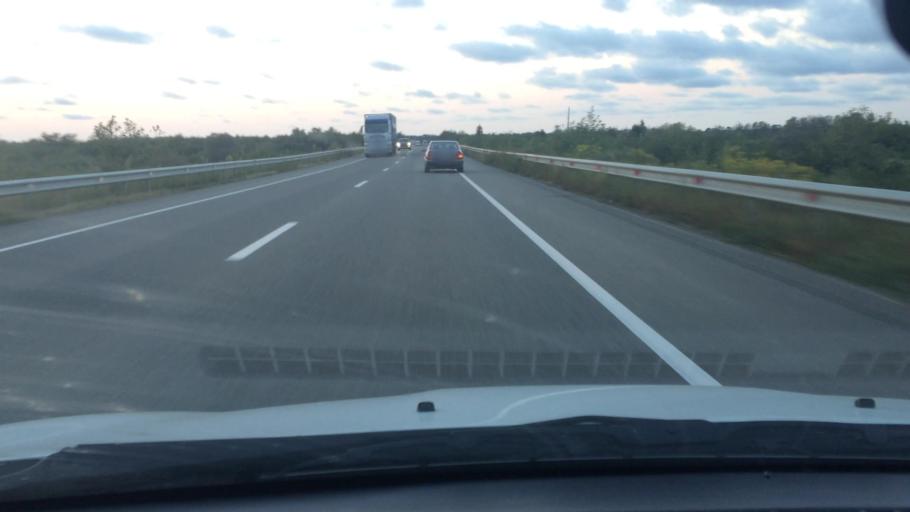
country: GE
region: Ajaria
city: Ochkhamuri
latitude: 41.9063
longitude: 41.7877
